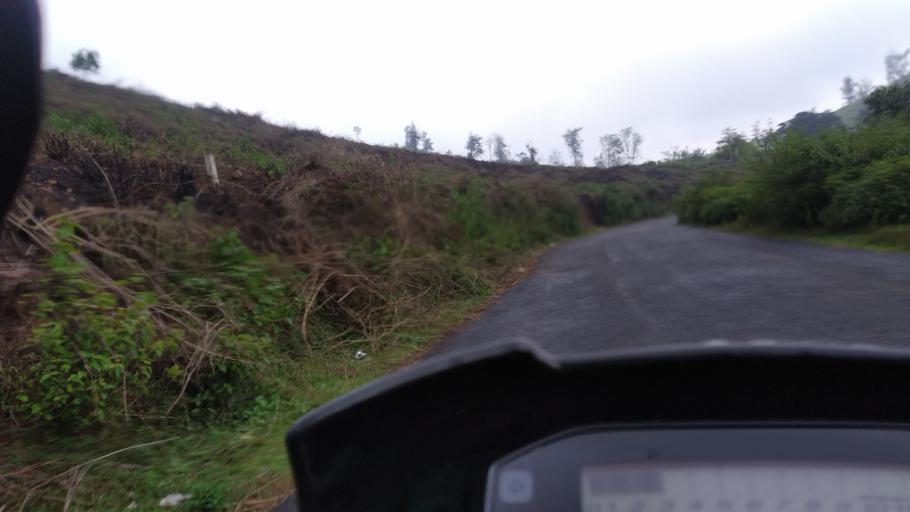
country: IN
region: Kerala
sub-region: Kottayam
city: Erattupetta
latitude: 9.6322
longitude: 76.9461
